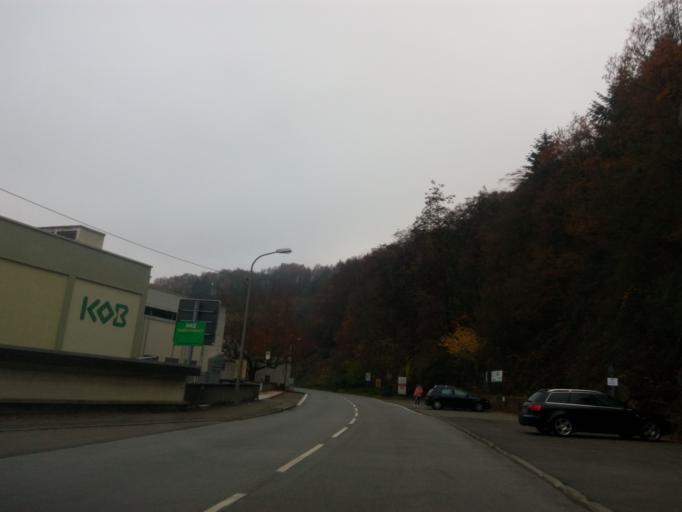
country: DE
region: Rheinland-Pfalz
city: Wolfstein
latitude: 49.5903
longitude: 7.6028
